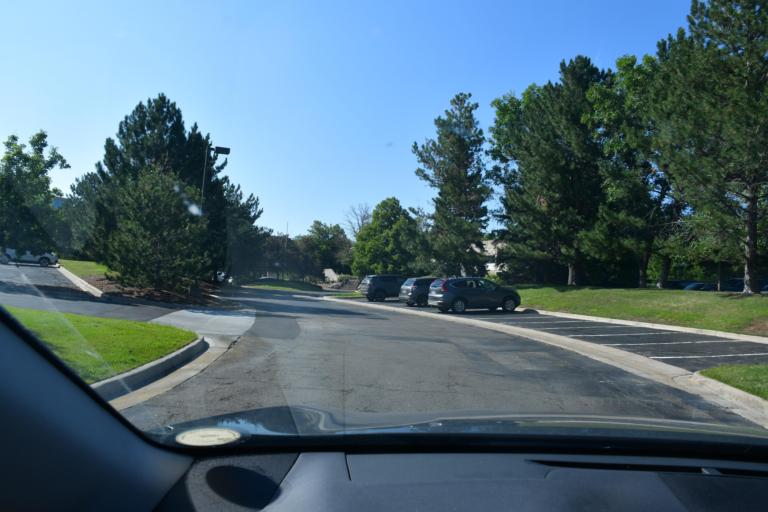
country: US
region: Colorado
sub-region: Douglas County
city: Meridian
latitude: 39.5679
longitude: -104.8635
